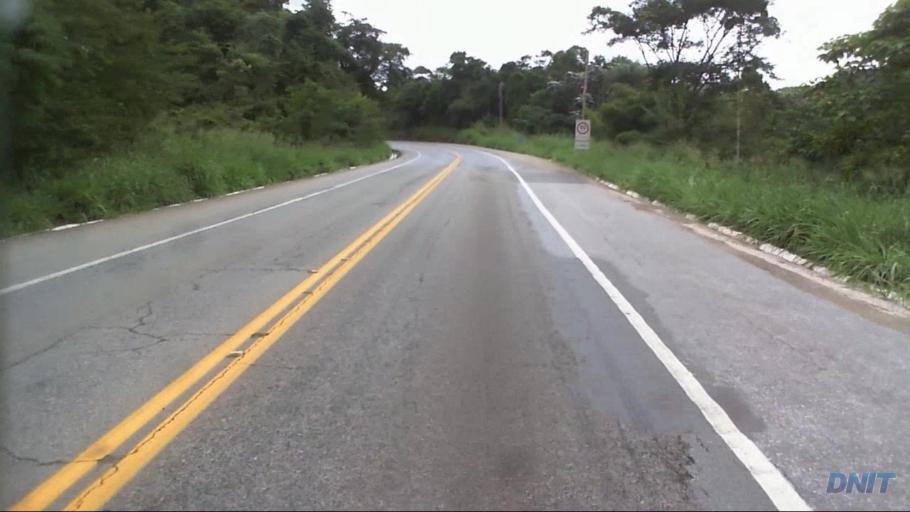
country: BR
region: Minas Gerais
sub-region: Barao De Cocais
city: Barao de Cocais
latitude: -19.8059
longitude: -43.4024
